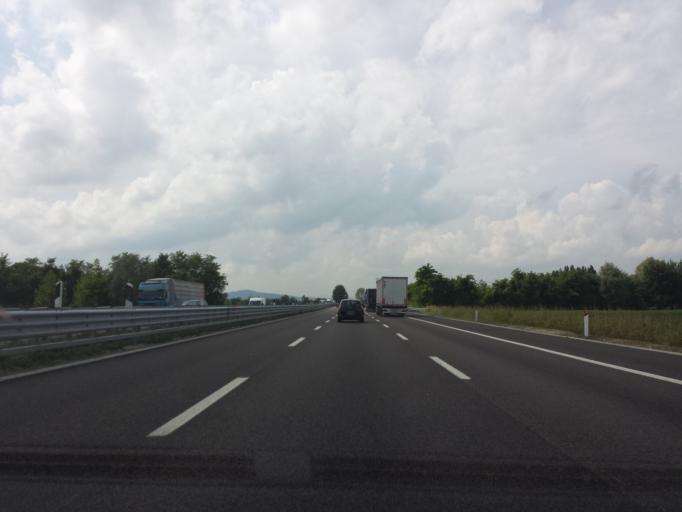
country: IT
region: Veneto
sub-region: Provincia di Padova
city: Arlesega
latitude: 45.4681
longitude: 11.7417
